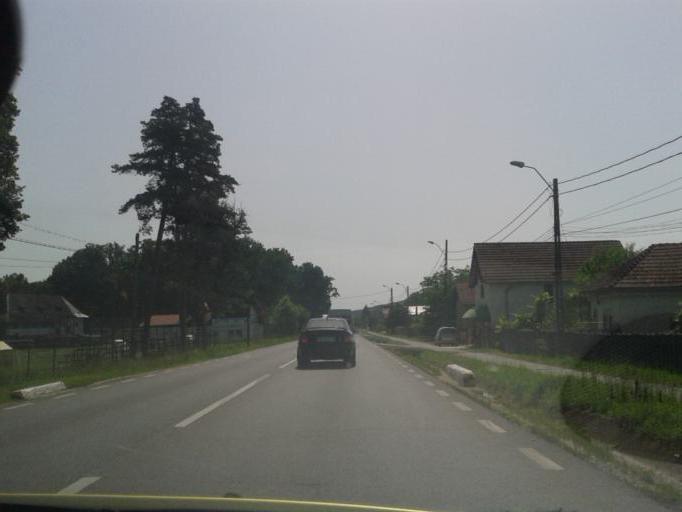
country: RO
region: Arges
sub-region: Comuna Bascov
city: Bascov
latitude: 44.8871
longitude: 24.7772
